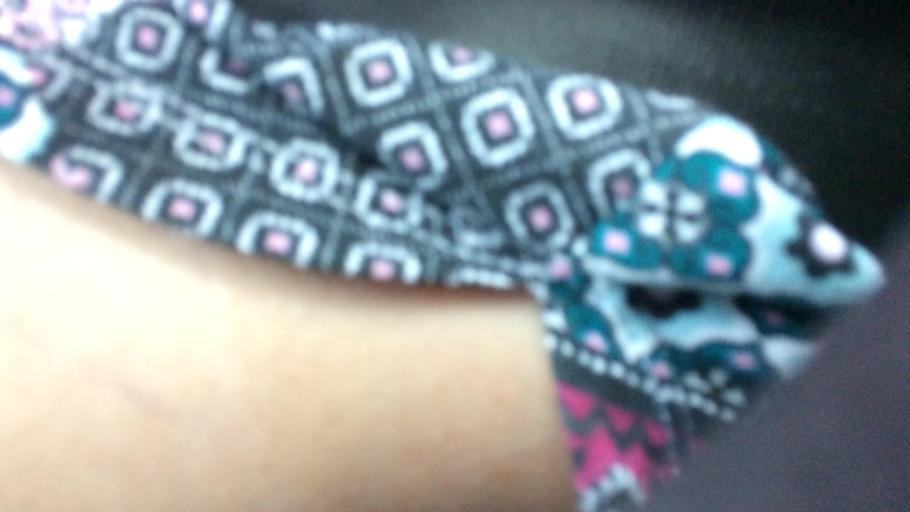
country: US
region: New Mexico
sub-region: Colfax County
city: Springer
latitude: 36.2118
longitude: -104.6615
